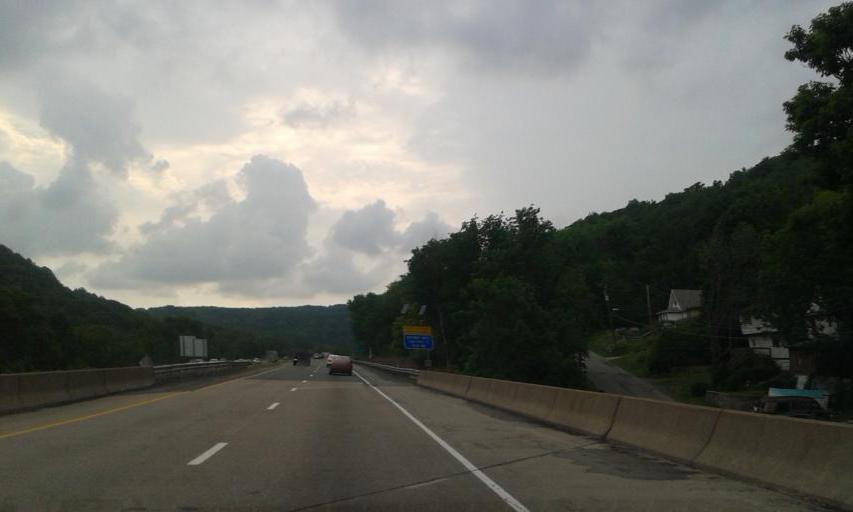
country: US
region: Pennsylvania
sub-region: Lackawanna County
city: Chinchilla
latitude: 41.4693
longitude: -75.6701
